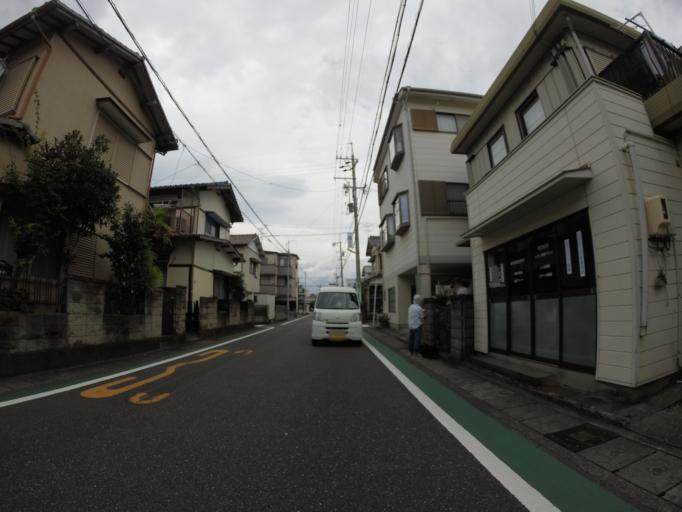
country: JP
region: Shizuoka
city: Shizuoka-shi
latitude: 34.9613
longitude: 138.4111
